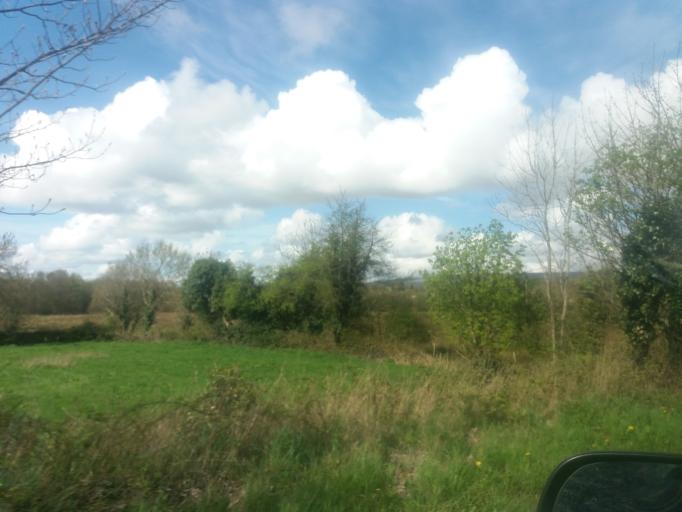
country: IE
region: Ulster
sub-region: An Cabhan
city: Belturbet
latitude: 54.1400
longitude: -7.5087
